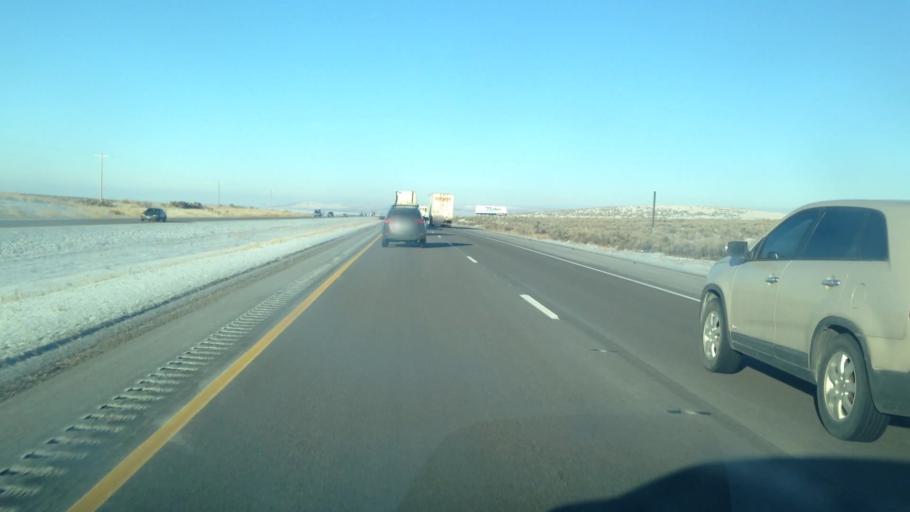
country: US
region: Idaho
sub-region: Bingham County
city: Fort Hall
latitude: 42.9831
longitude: -112.4193
